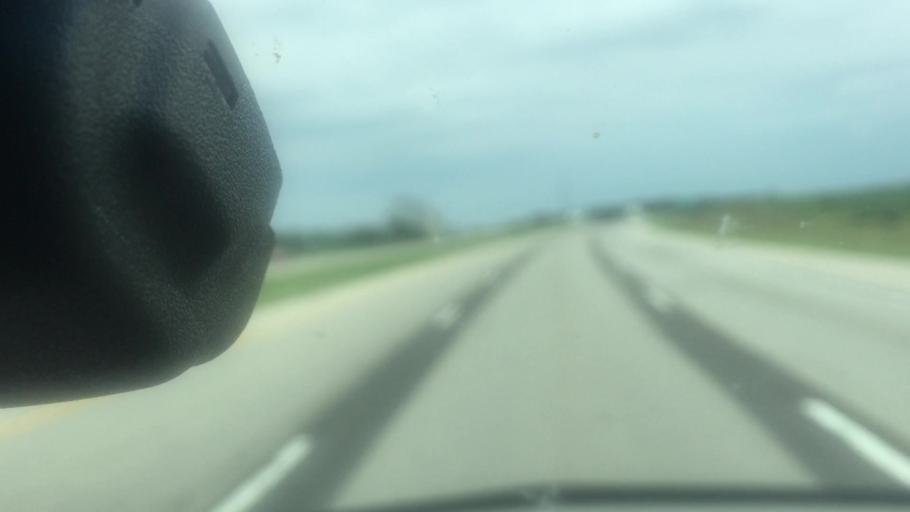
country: US
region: Illinois
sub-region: Sangamon County
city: Williamsville
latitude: 40.0288
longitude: -89.4783
